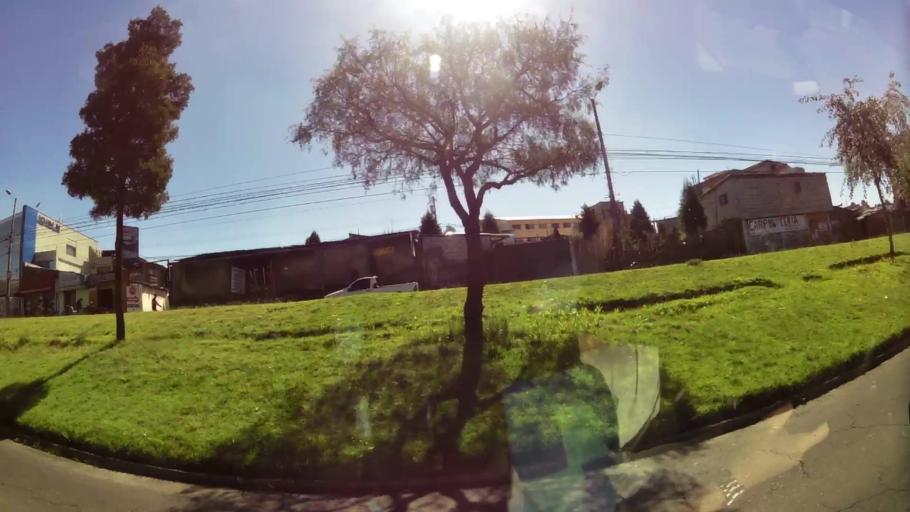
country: EC
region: Pichincha
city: Quito
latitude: -0.1486
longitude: -78.4684
